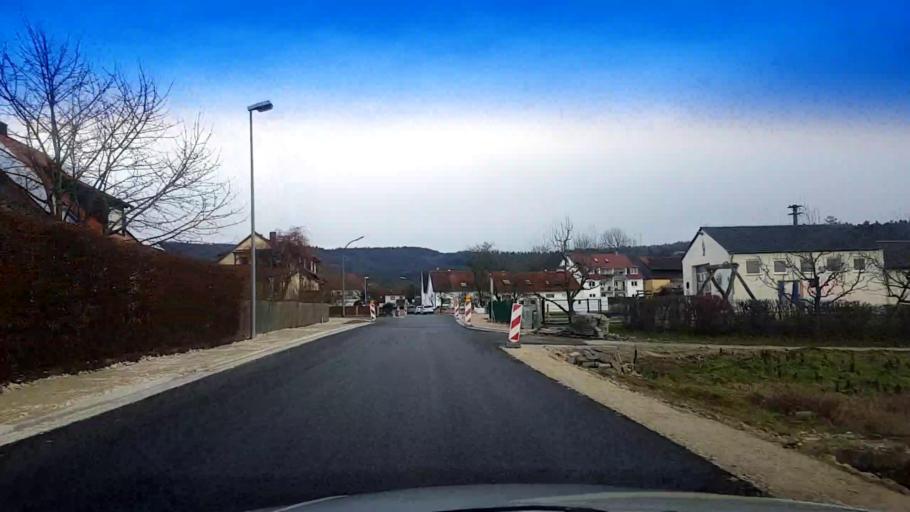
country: DE
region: Bavaria
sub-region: Upper Franconia
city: Litzendorf
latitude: 49.9391
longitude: 11.0080
